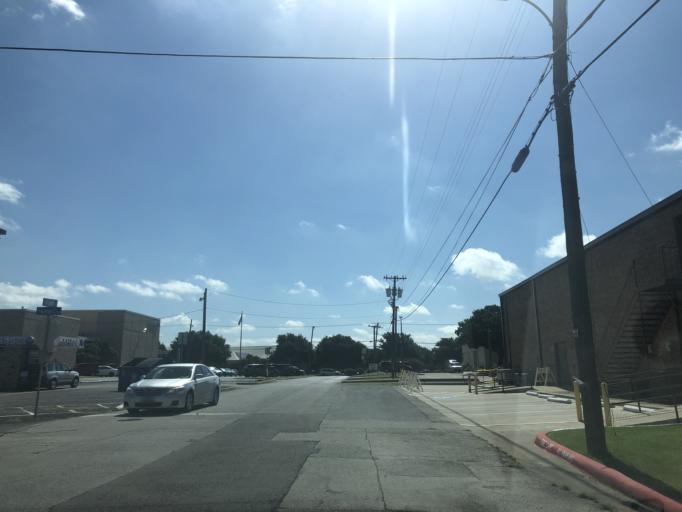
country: US
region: Texas
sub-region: Dallas County
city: Duncanville
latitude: 32.6490
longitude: -96.9099
